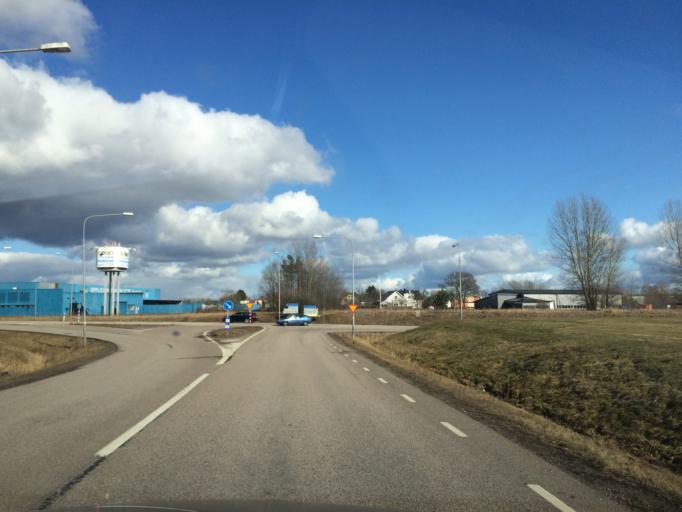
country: SE
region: Vaestra Goetaland
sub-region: Skara Kommun
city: Skara
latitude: 58.3765
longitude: 13.4110
